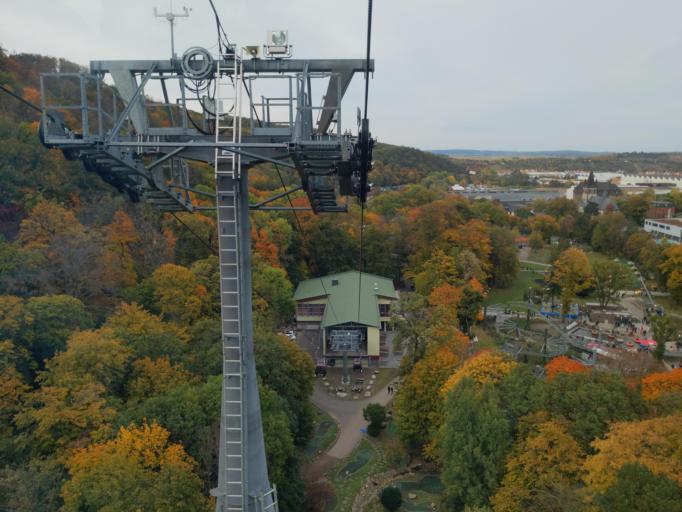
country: DE
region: Saxony-Anhalt
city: Thale
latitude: 51.7402
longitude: 11.0268
